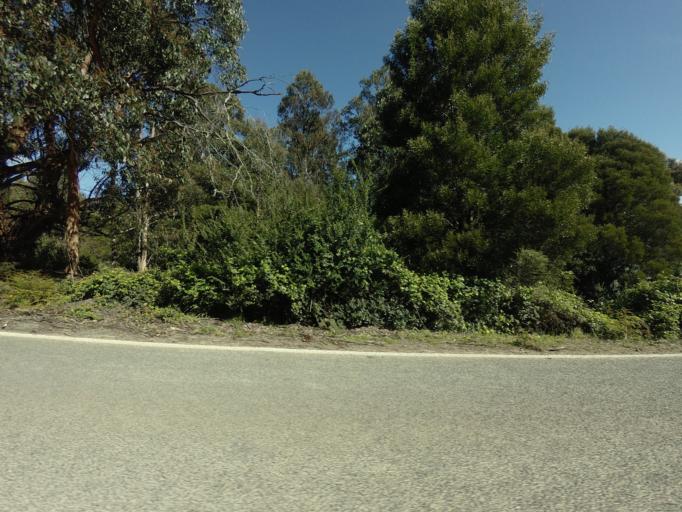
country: AU
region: Tasmania
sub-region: Derwent Valley
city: New Norfolk
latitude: -42.7063
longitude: 146.7114
